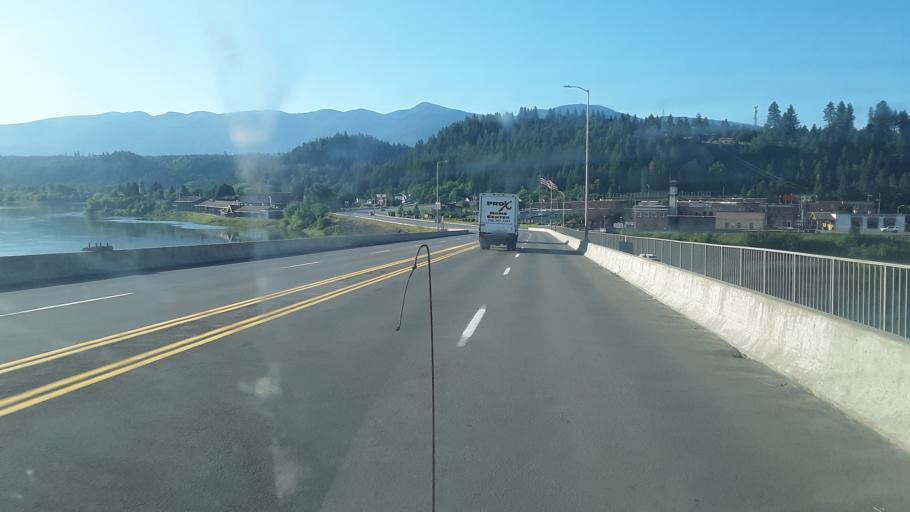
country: US
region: Idaho
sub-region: Boundary County
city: Bonners Ferry
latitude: 48.7002
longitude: -116.3136
